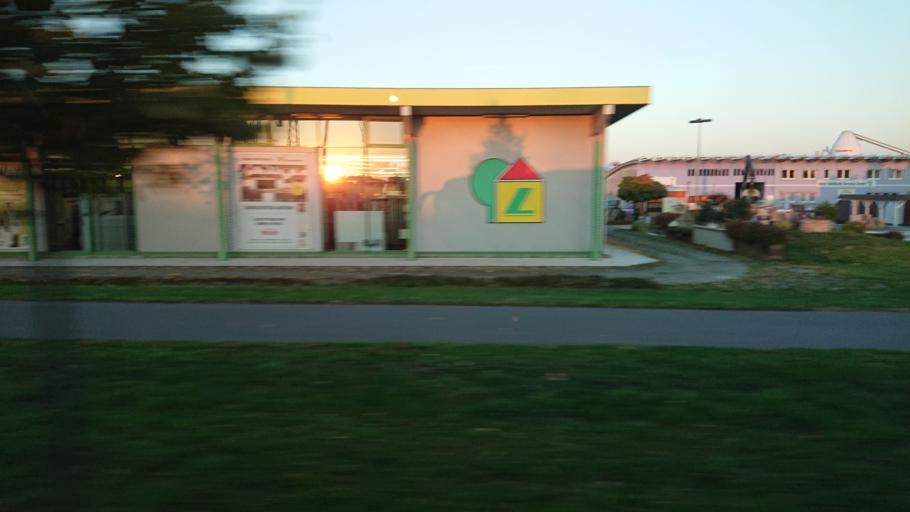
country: DE
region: Mecklenburg-Vorpommern
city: Greifswald
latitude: 54.0719
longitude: 13.3806
